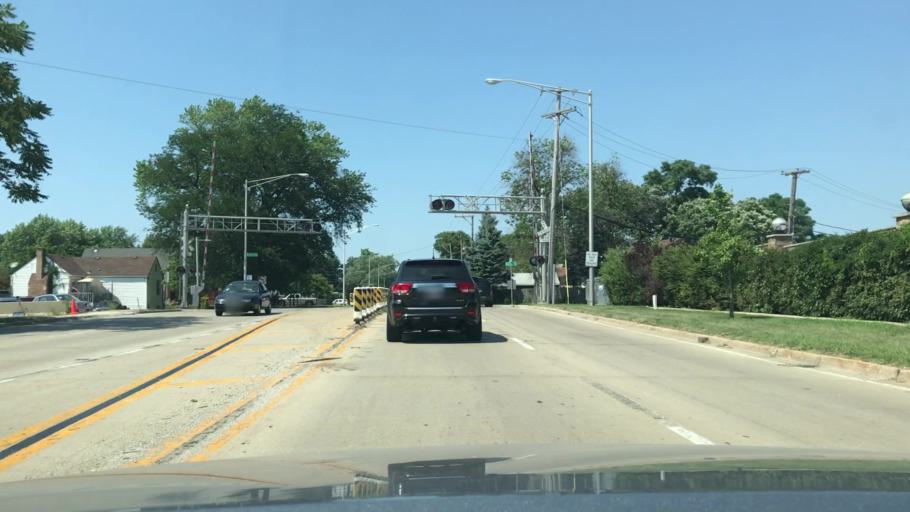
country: US
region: Illinois
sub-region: Cook County
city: Oak Lawn
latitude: 41.7145
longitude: -87.7601
